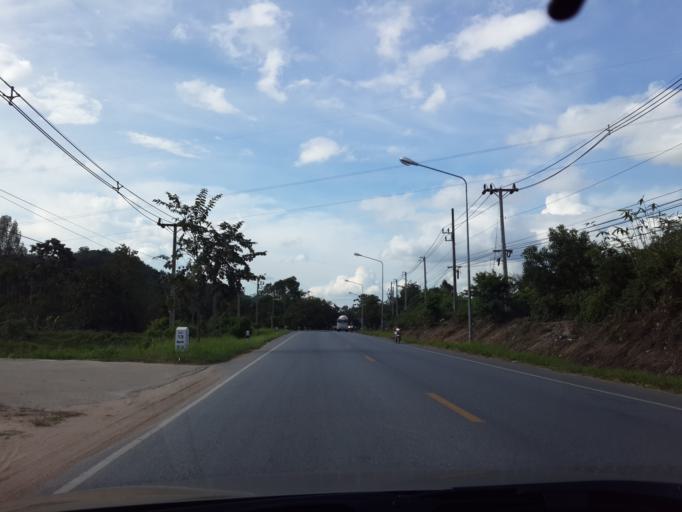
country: TH
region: Yala
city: Krong Pi Nang
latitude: 6.4668
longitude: 101.3276
